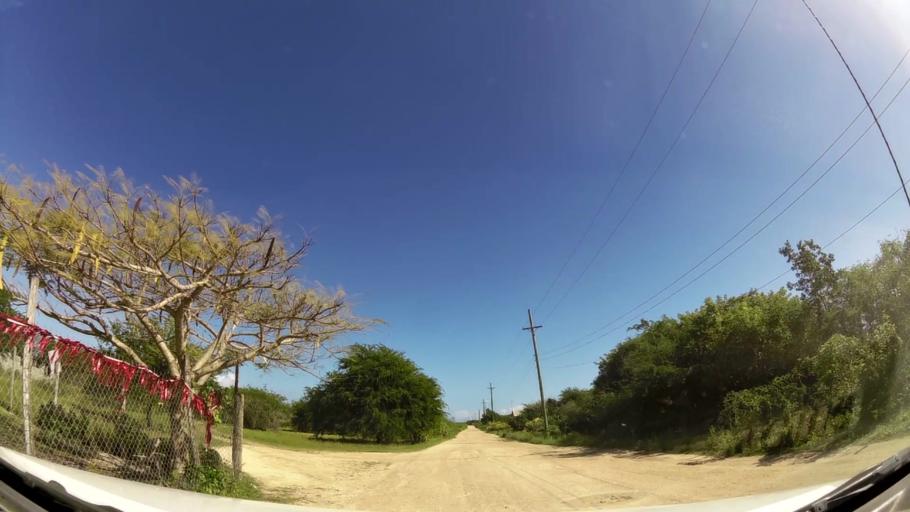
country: AG
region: Barbuda
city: Codrington
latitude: 17.6498
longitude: -61.8171
